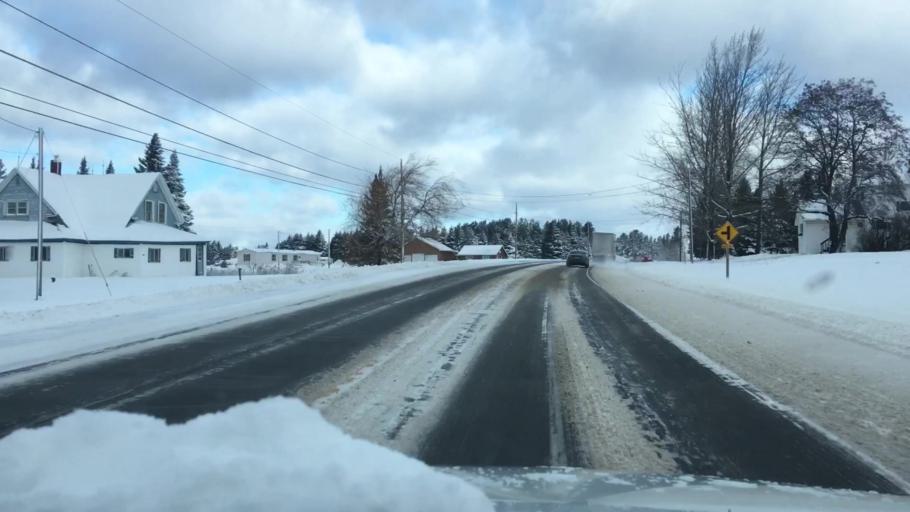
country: US
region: Maine
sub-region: Aroostook County
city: Caribou
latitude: 46.7901
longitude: -67.9907
